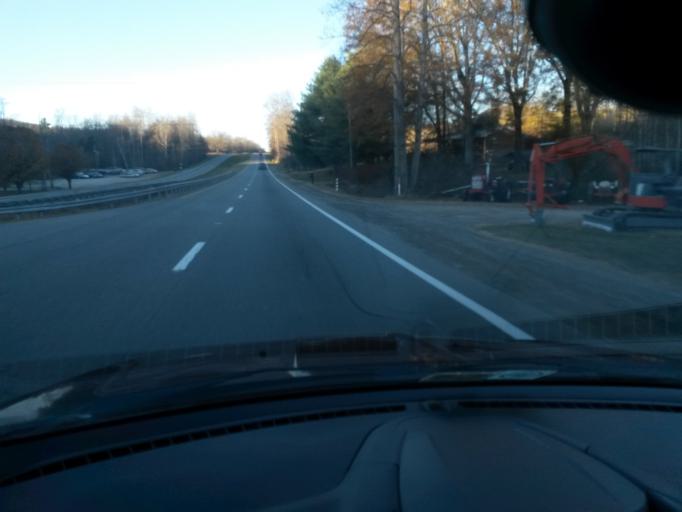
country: US
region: Virginia
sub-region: Franklin County
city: Henry Fork
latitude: 36.8500
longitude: -79.8839
